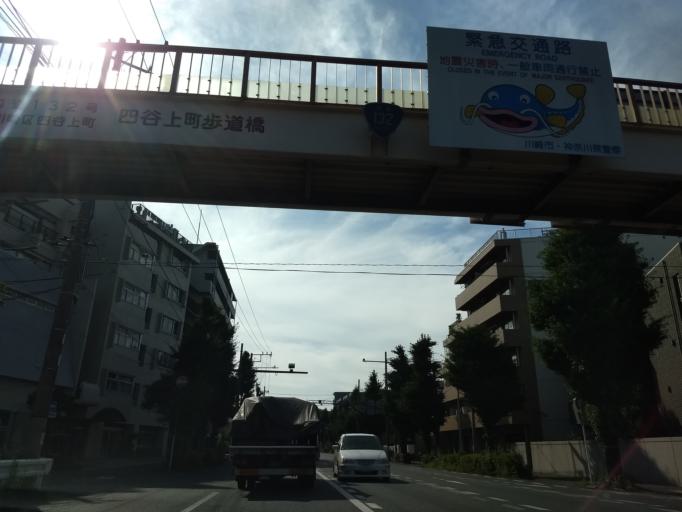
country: JP
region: Kanagawa
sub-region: Kawasaki-shi
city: Kawasaki
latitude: 35.5291
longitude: 139.7371
